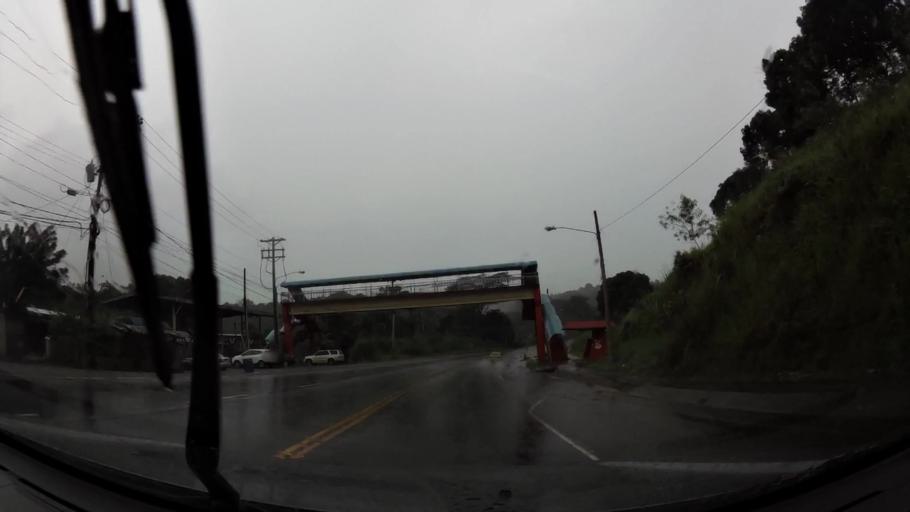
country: PA
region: Colon
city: Gatun
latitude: 9.2910
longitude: -79.7705
